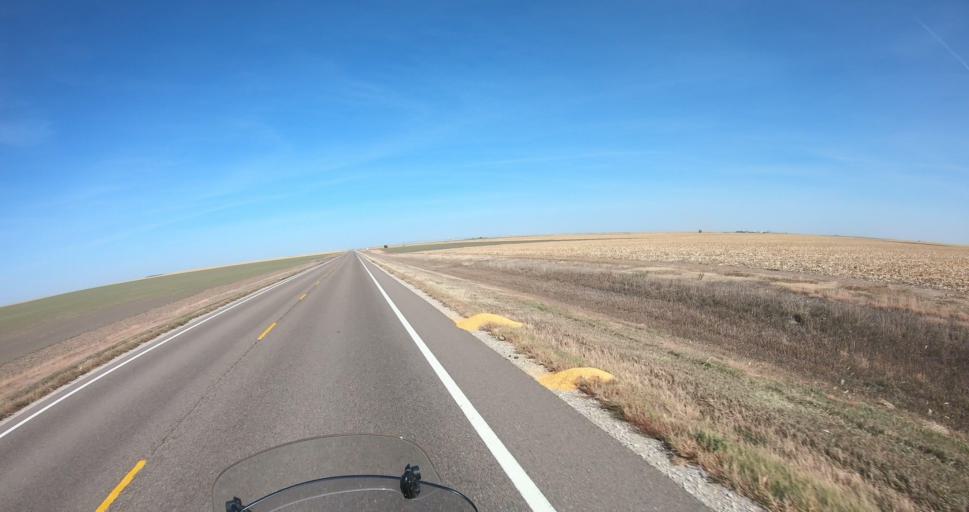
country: US
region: Kansas
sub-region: Thomas County
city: Colby
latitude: 39.4127
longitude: -100.8709
